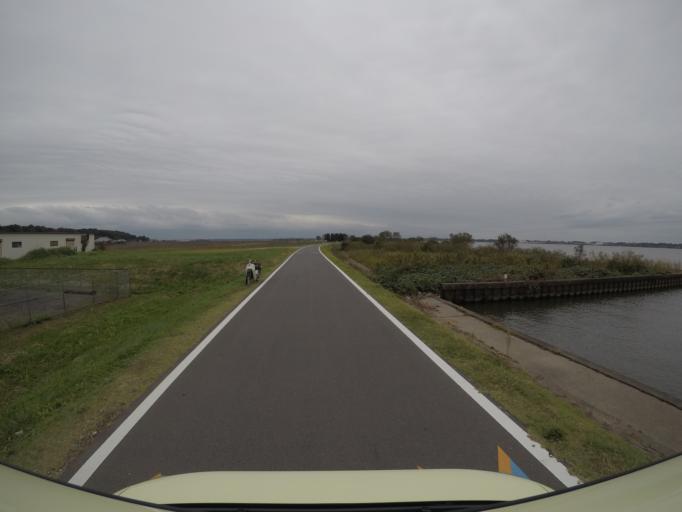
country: JP
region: Ibaraki
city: Ami
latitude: 36.0800
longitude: 140.2388
